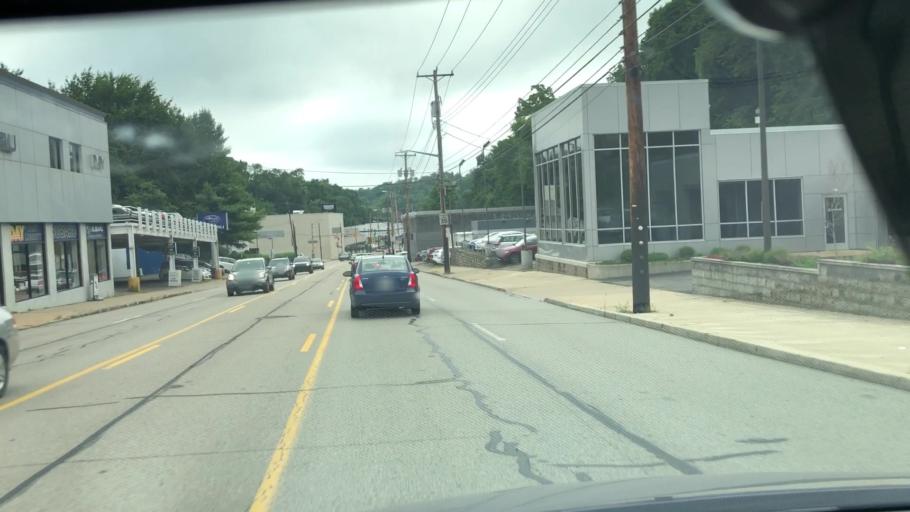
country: US
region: Pennsylvania
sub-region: Allegheny County
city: Dormont
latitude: 40.4003
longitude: -80.0236
